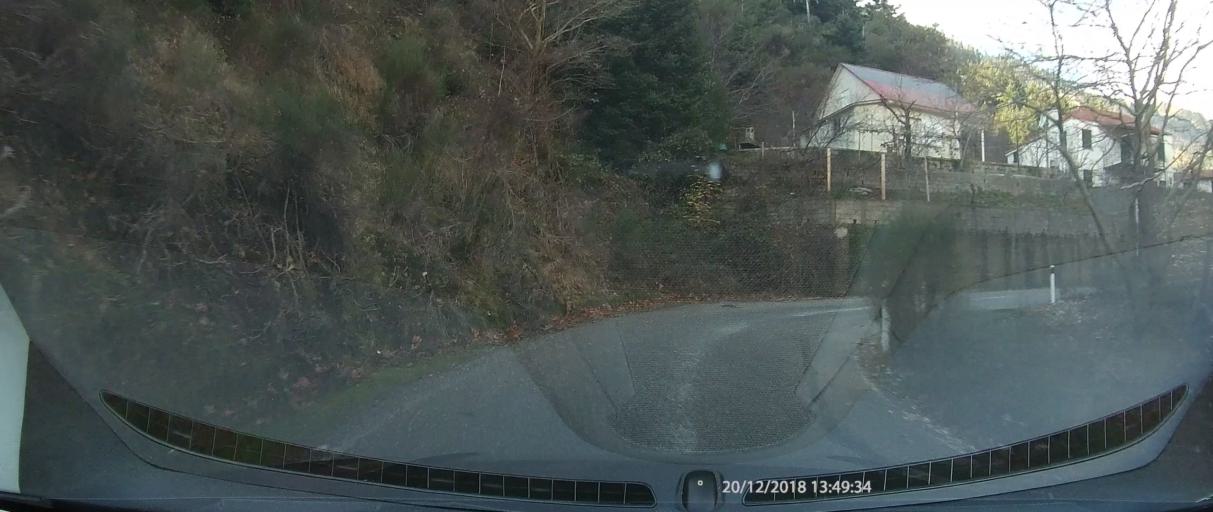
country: GR
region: West Greece
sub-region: Nomos Aitolias kai Akarnanias
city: Paravola
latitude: 38.6932
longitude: 21.6071
